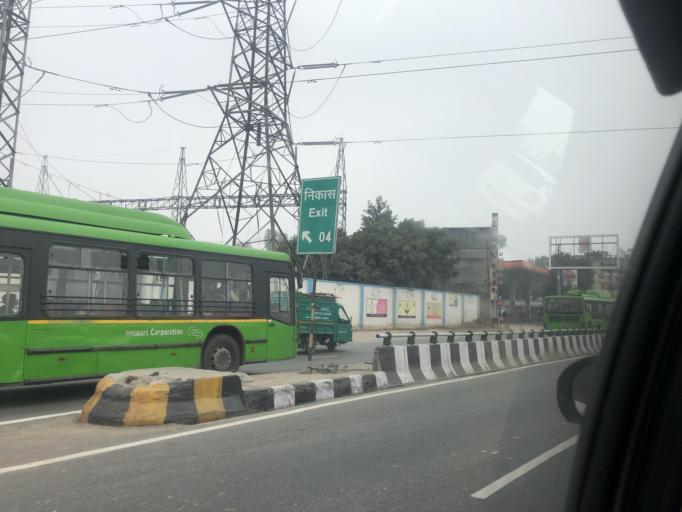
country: IN
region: Haryana
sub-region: Gurgaon
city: Gurgaon
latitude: 28.5257
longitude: 77.1011
